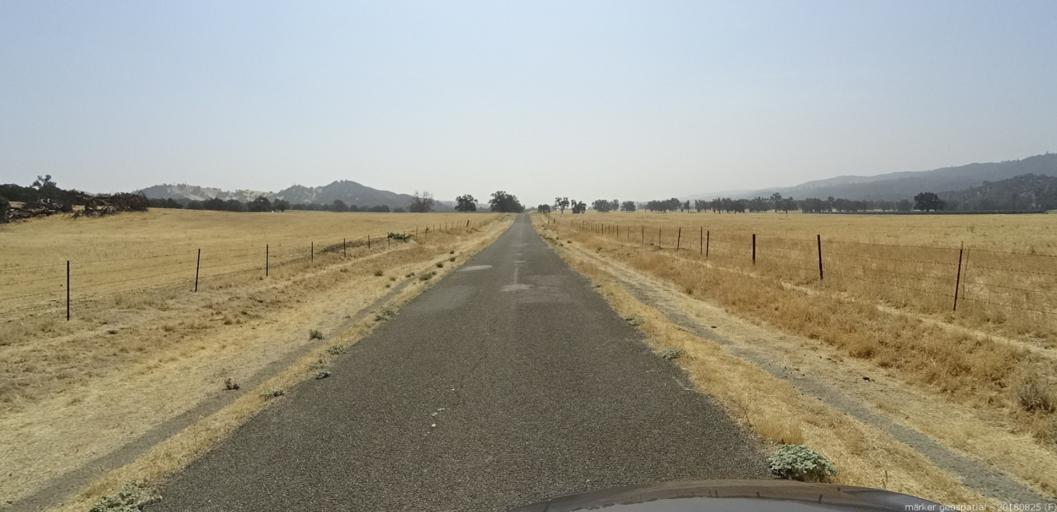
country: US
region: California
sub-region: Fresno County
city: Coalinga
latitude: 35.9542
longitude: -120.5367
